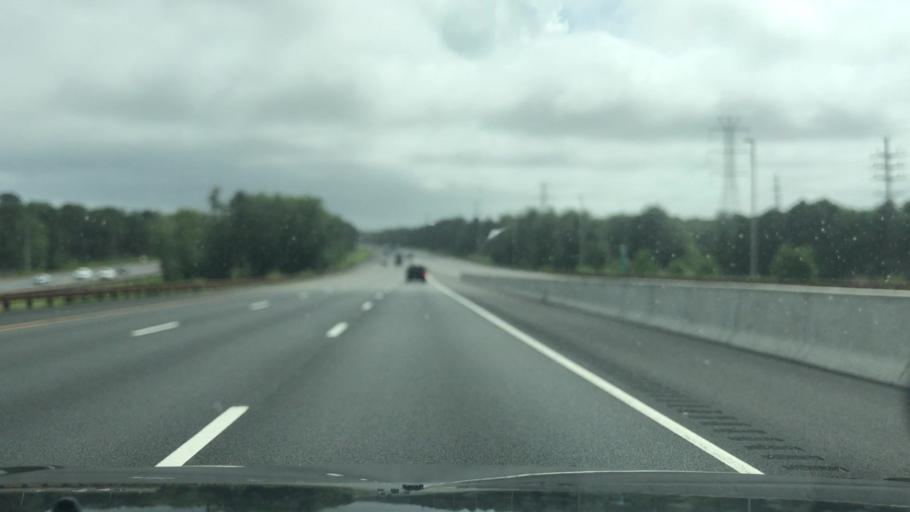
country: US
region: New Jersey
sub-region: Ocean County
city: Leisure Village
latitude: 40.0527
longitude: -74.1702
